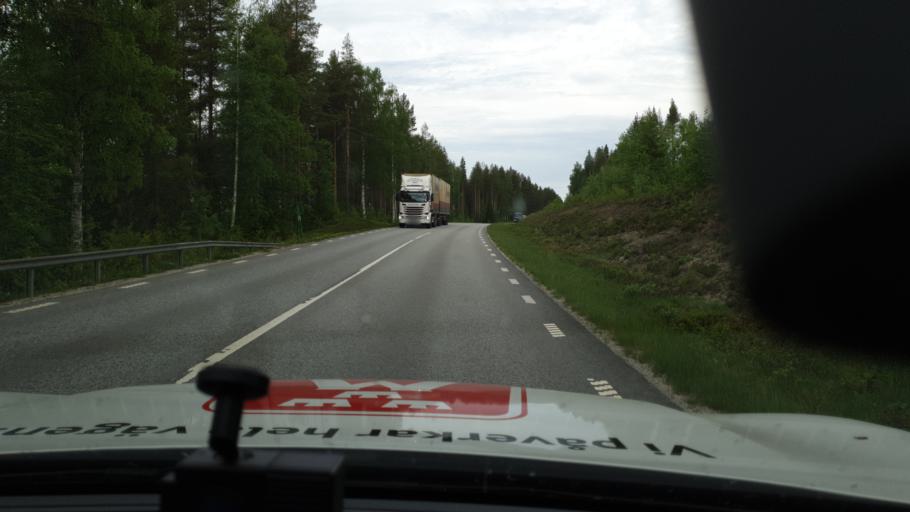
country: SE
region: Vaesterbotten
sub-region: Lycksele Kommun
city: Lycksele
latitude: 64.5486
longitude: 18.7391
